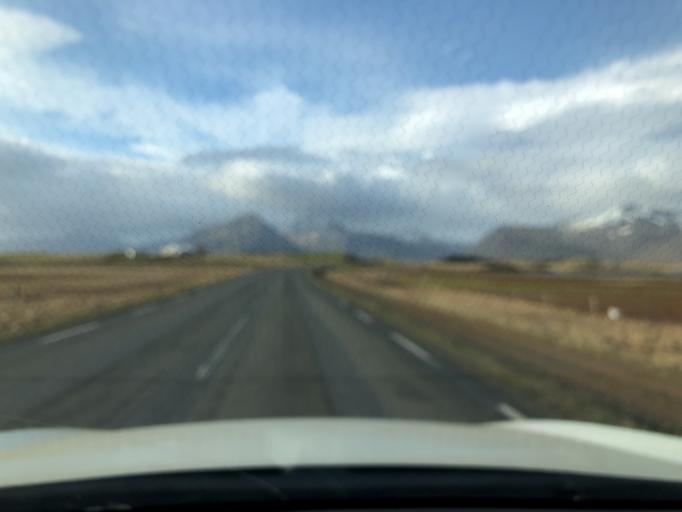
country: IS
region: East
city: Hoefn
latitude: 64.2725
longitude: -15.2023
